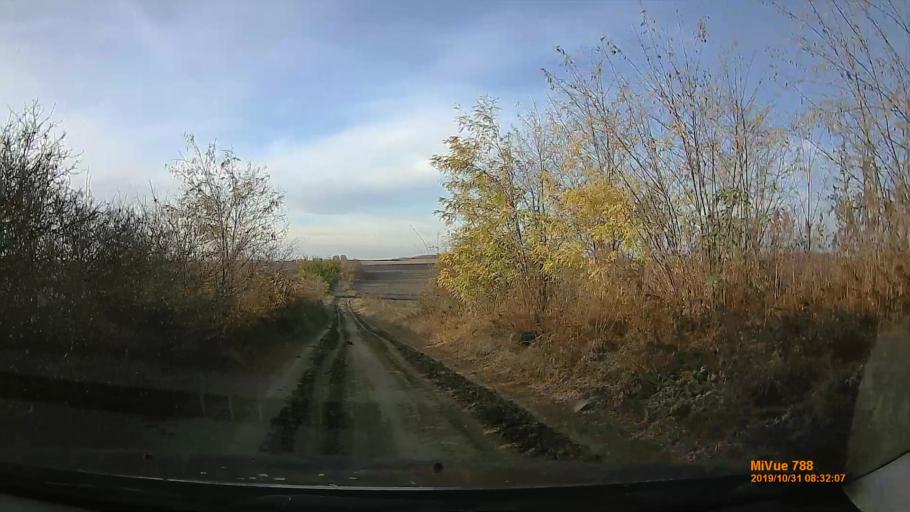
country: HU
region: Pest
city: Tapiobicske
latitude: 47.3444
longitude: 19.6638
